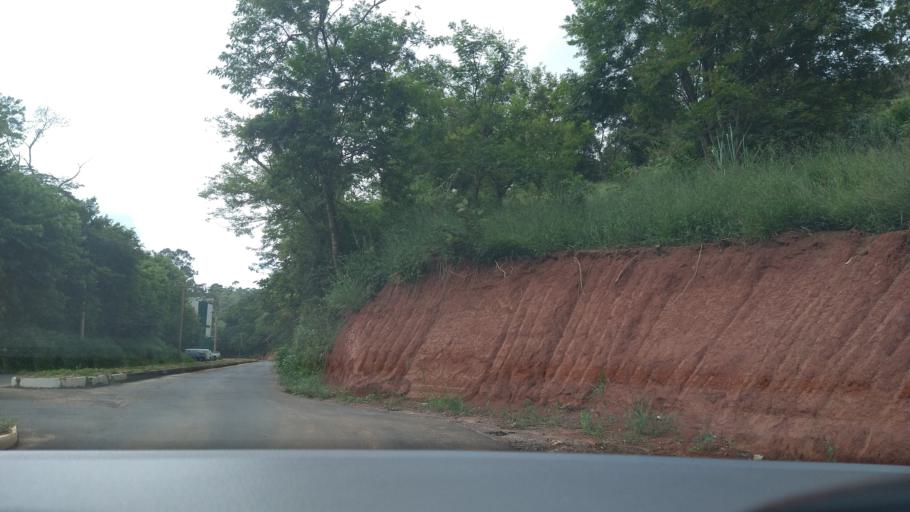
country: BR
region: Minas Gerais
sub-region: Vicosa
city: Vicosa
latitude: -20.7786
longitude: -42.8527
